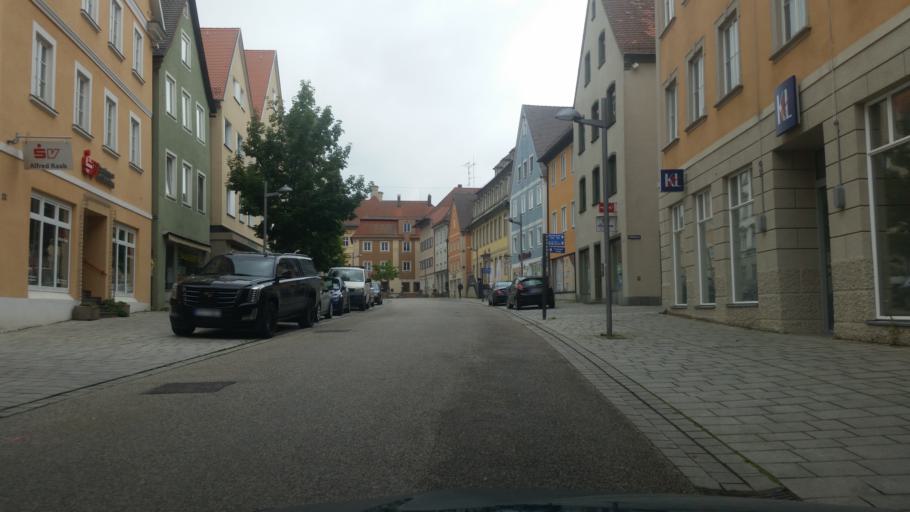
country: DE
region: Baden-Wuerttemberg
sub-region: Regierungsbezirk Stuttgart
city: Ellwangen
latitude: 48.9609
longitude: 10.1322
